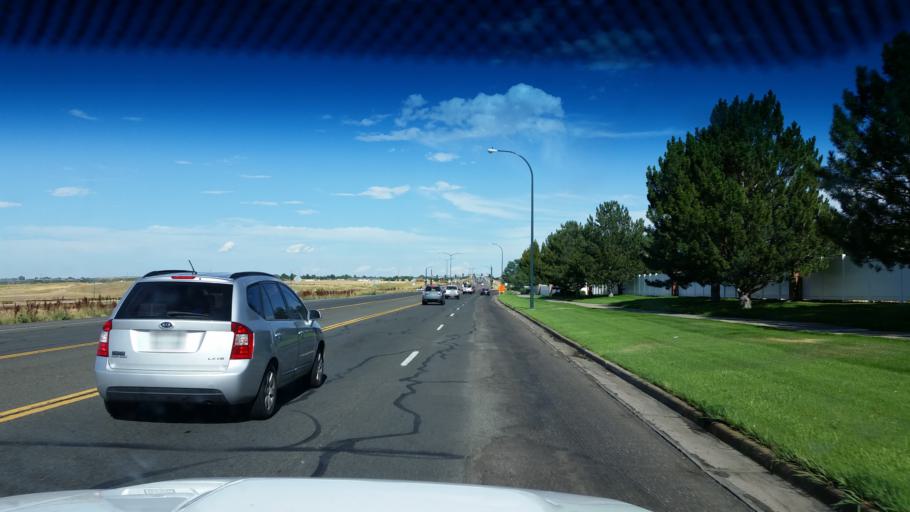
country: US
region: Colorado
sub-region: Adams County
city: Northglenn
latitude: 39.9285
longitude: -105.0008
